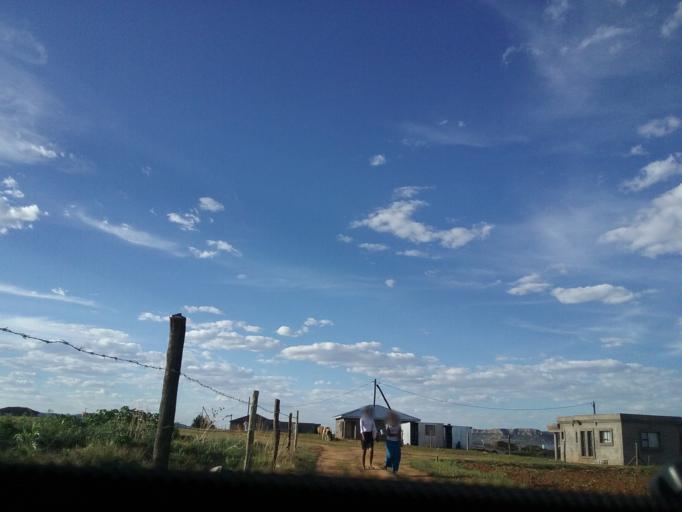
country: LS
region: Maseru
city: Maseru
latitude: -29.4282
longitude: 27.5698
